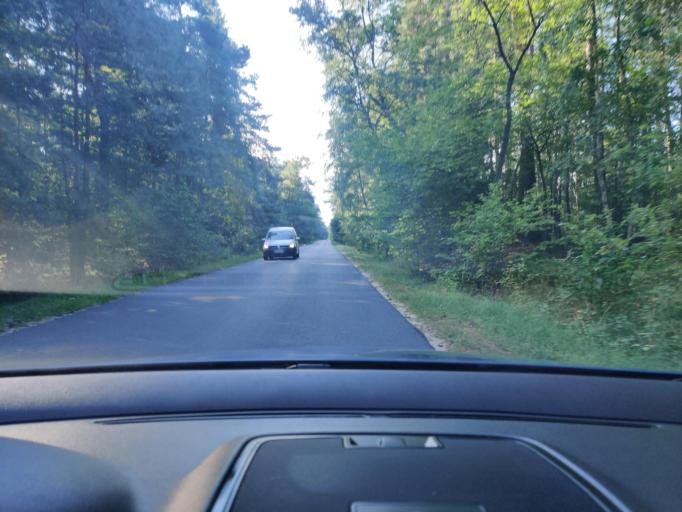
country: PL
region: Greater Poland Voivodeship
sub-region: Konin
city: Konin
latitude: 52.1832
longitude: 18.3320
